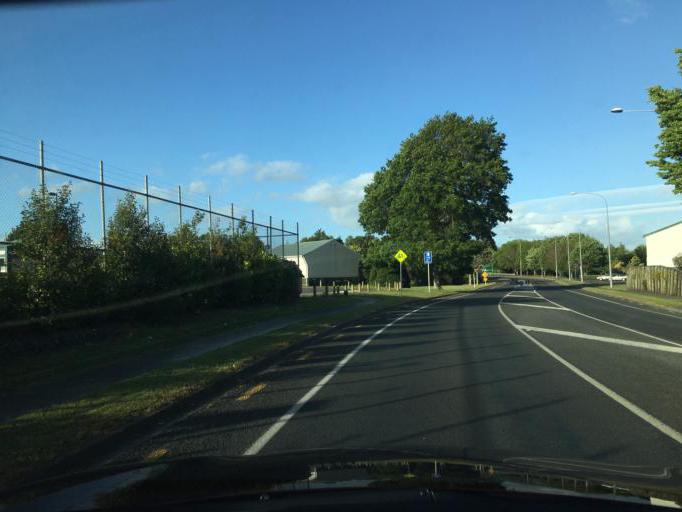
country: NZ
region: Waikato
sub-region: Waipa District
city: Cambridge
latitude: -38.0097
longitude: 175.3290
